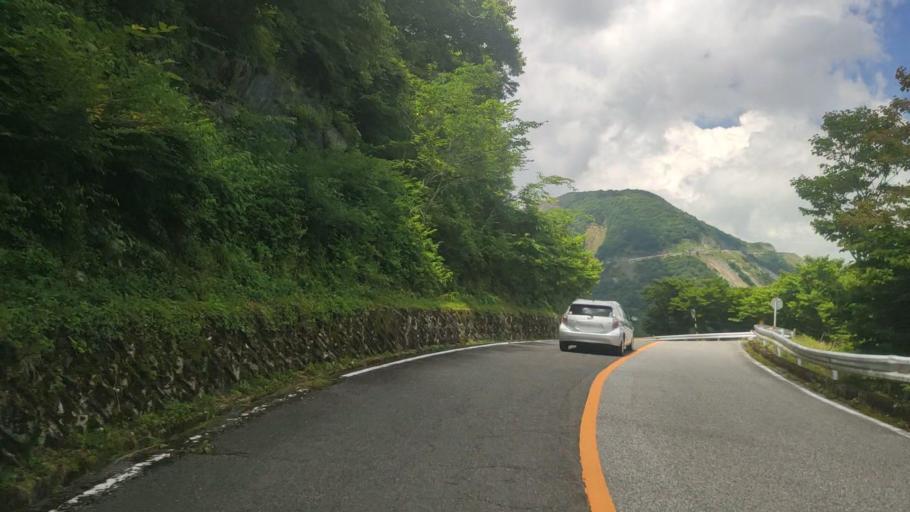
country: JP
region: Gifu
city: Tarui
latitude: 35.4160
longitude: 136.4207
